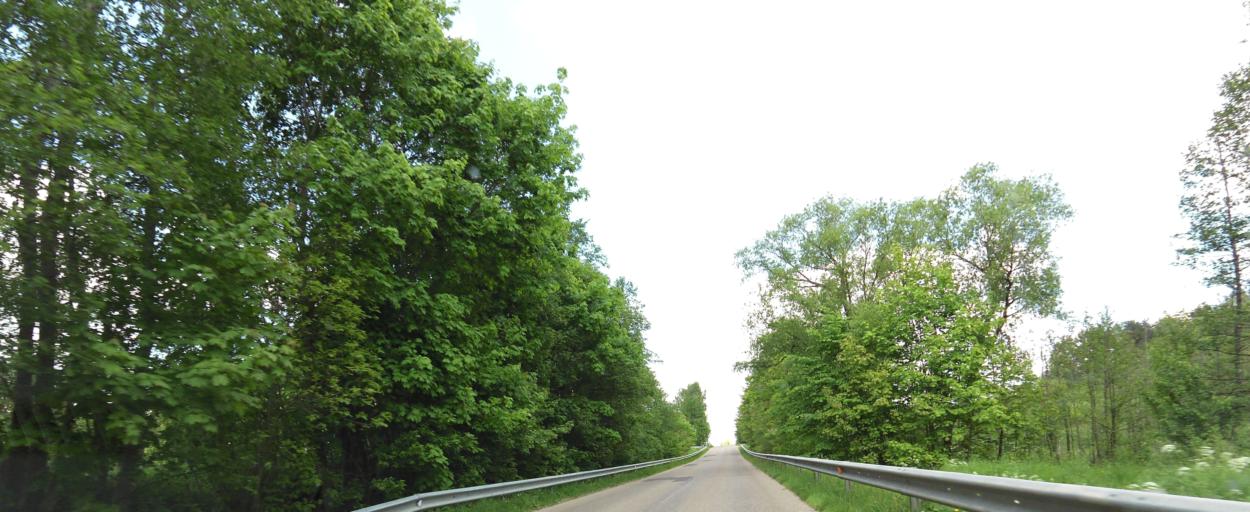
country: LT
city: Trakai
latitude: 54.6806
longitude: 24.9534
